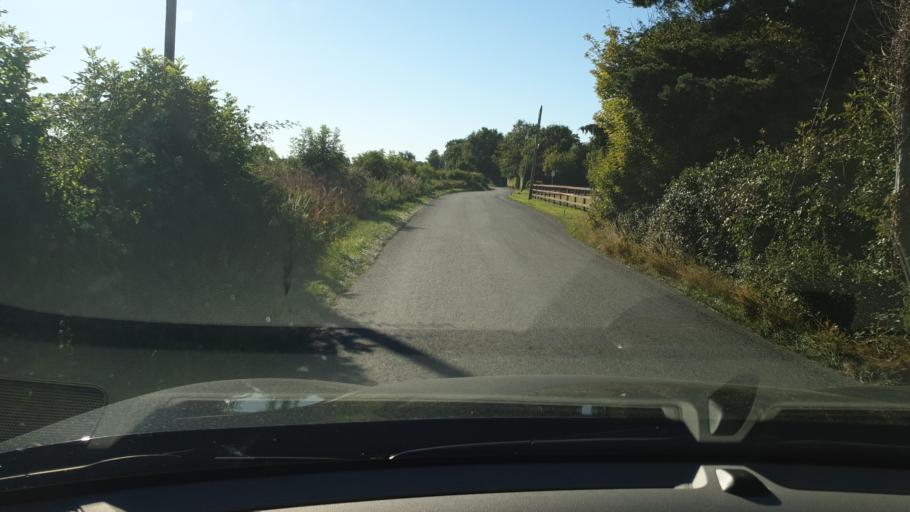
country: IE
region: Leinster
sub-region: An Mhi
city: Ashbourne
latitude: 53.4581
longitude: -6.3618
